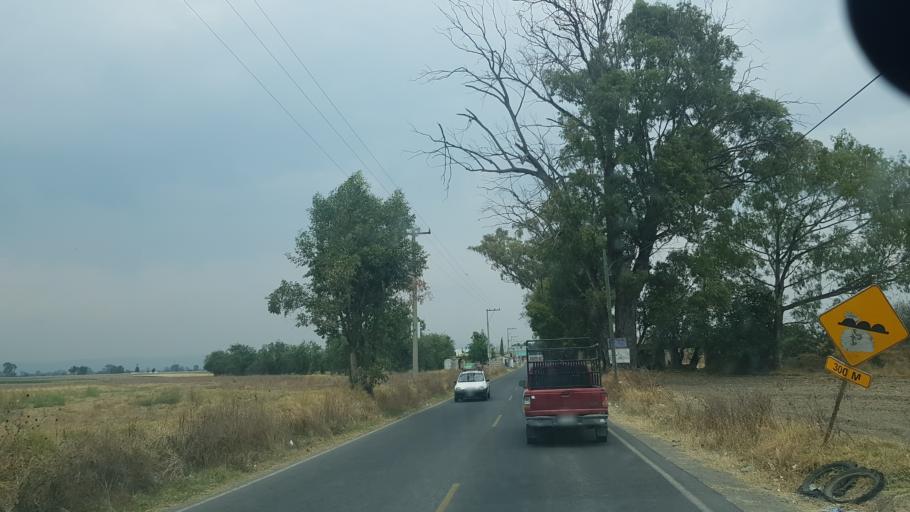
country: MX
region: Puebla
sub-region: Huejotzingo
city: San Mateo Capultitlan
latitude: 19.2011
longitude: -98.4351
